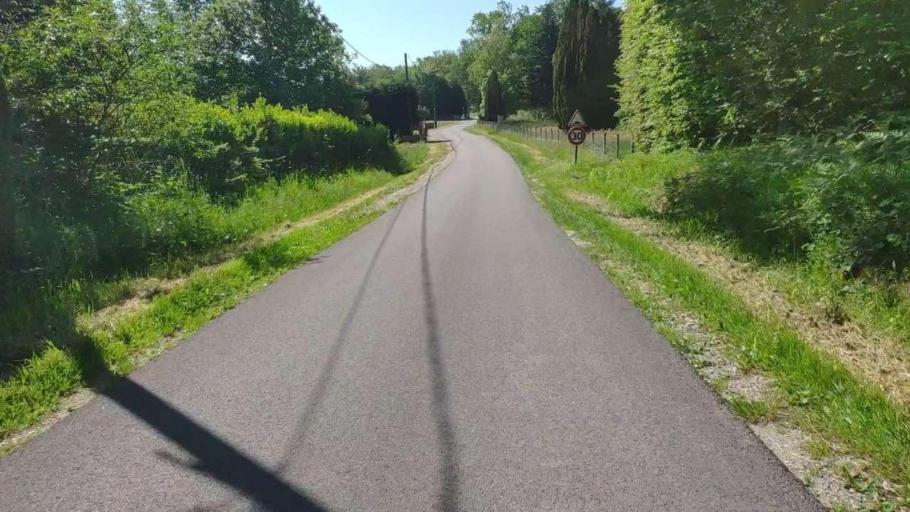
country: FR
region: Franche-Comte
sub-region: Departement du Jura
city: Bletterans
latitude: 46.7991
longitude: 5.4452
